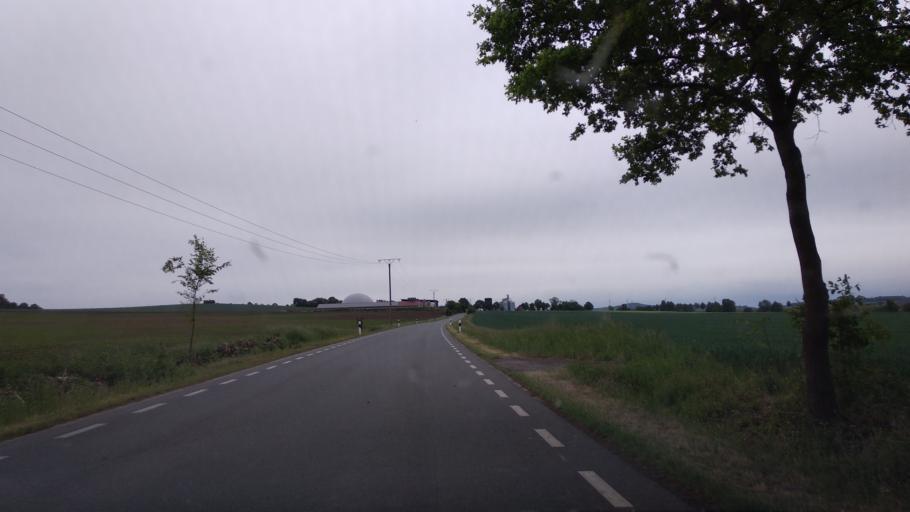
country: DE
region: North Rhine-Westphalia
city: Borgentreich
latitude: 51.5433
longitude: 9.2267
